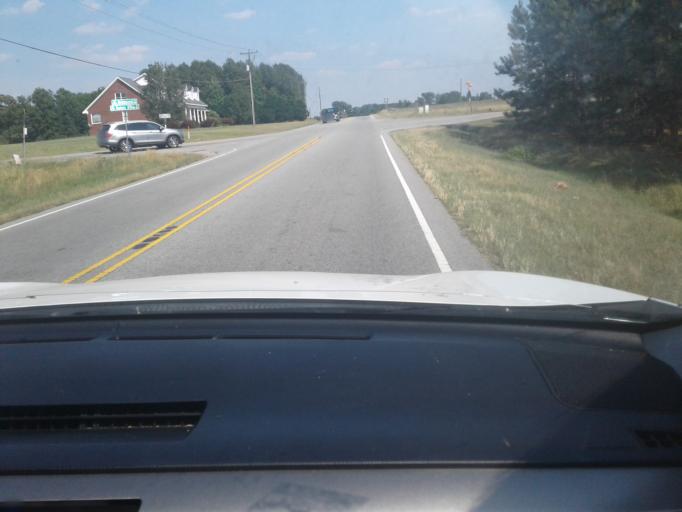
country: US
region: North Carolina
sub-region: Johnston County
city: Benson
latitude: 35.3970
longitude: -78.5971
